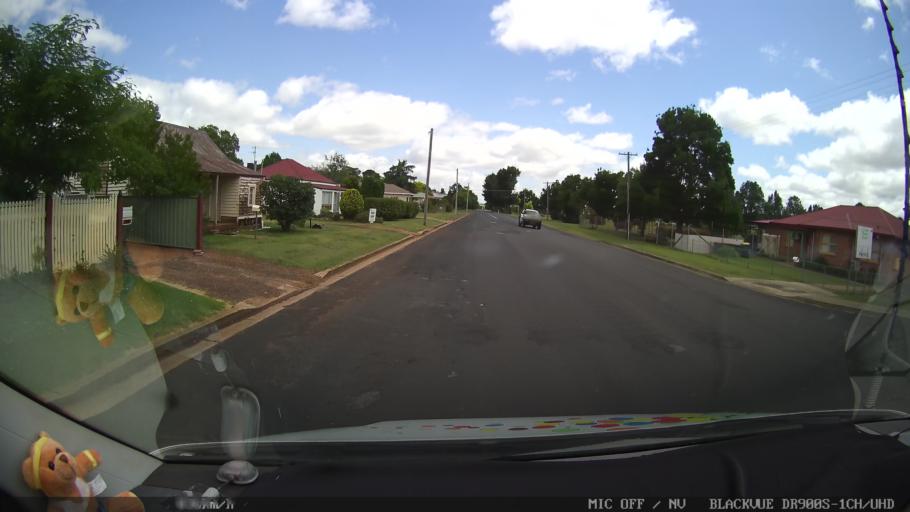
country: AU
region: New South Wales
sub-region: Glen Innes Severn
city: Glen Innes
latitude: -29.7320
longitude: 151.7334
